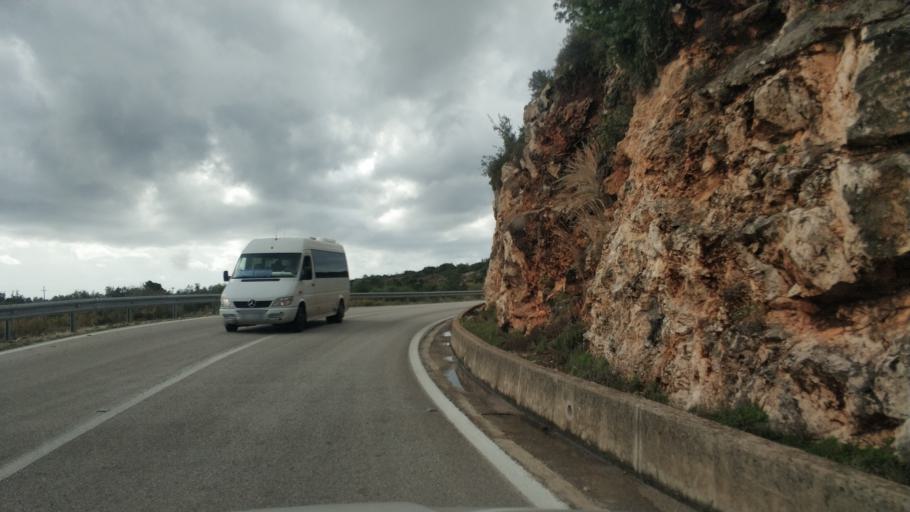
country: AL
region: Vlore
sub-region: Rrethi i Vlores
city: Vranisht
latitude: 40.1448
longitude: 19.6555
